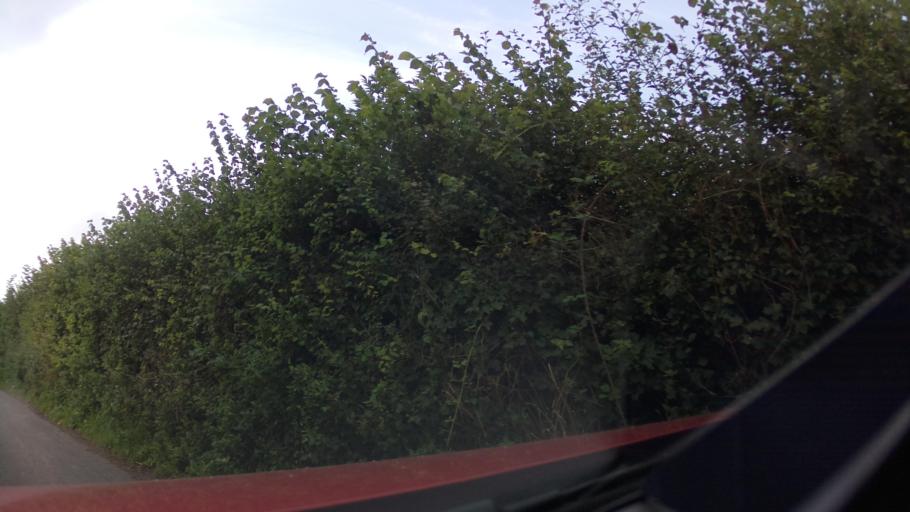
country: GB
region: England
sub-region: Somerset
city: Evercreech
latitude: 51.1462
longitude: -2.4903
